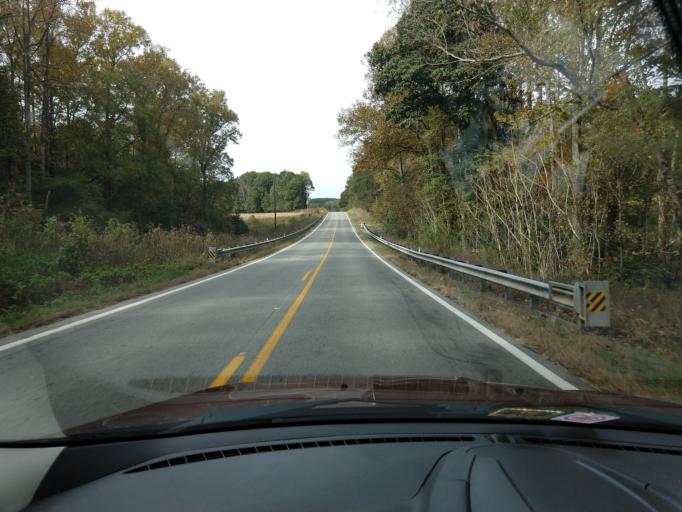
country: US
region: Virginia
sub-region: Pittsylvania County
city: Gretna
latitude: 36.9452
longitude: -79.4773
